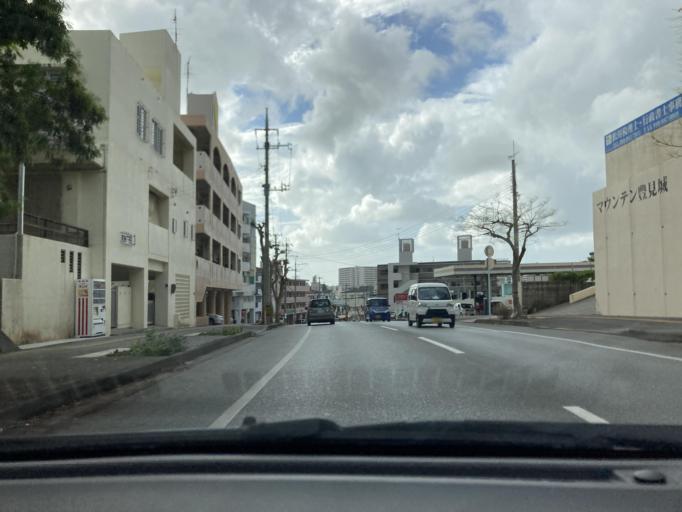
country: JP
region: Okinawa
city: Tomigusuku
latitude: 26.1825
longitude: 127.6798
